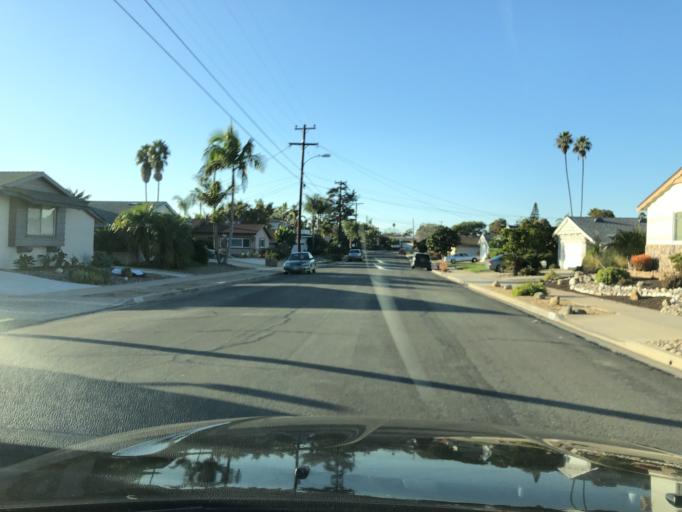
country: US
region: California
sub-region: San Diego County
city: La Jolla
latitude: 32.8236
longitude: -117.1908
